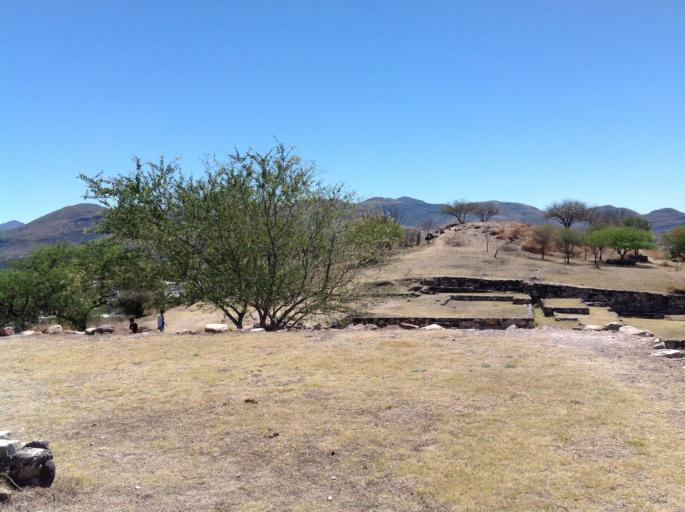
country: MX
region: Oaxaca
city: Ciudad de Huajuapam de Leon
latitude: 17.8188
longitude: -97.7735
